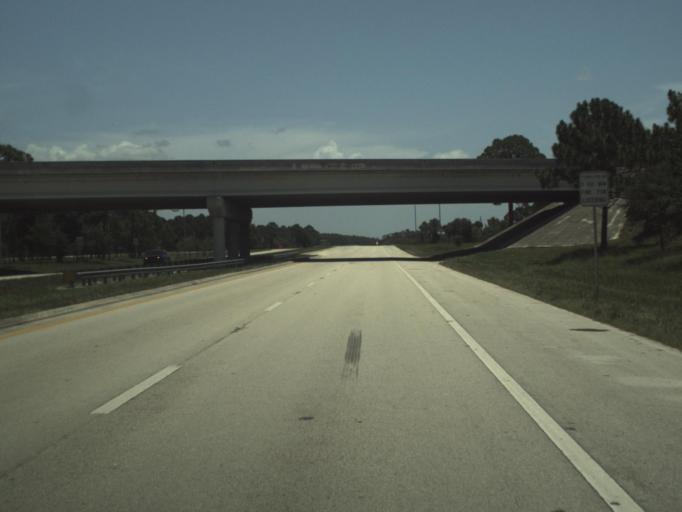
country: US
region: Florida
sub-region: Martin County
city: Palm City
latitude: 27.1615
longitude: -80.3902
